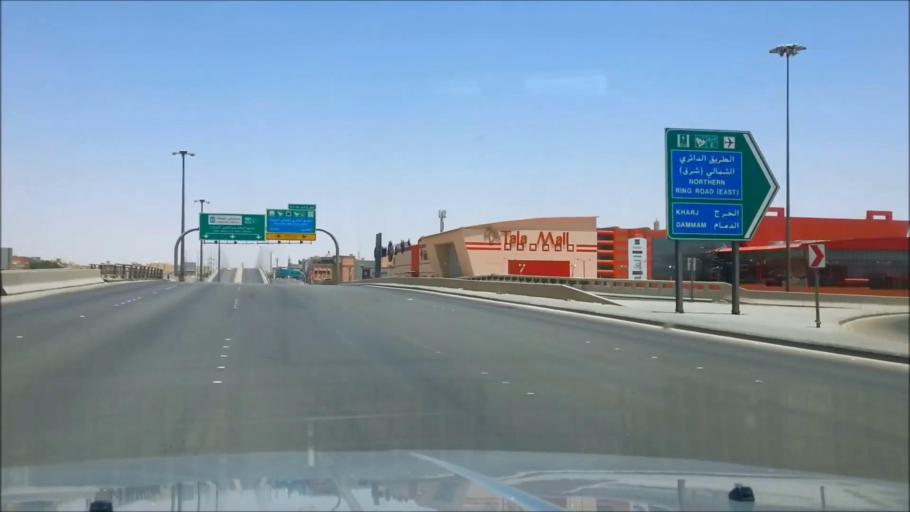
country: SA
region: Ar Riyad
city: Riyadh
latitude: 24.7672
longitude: 46.6699
